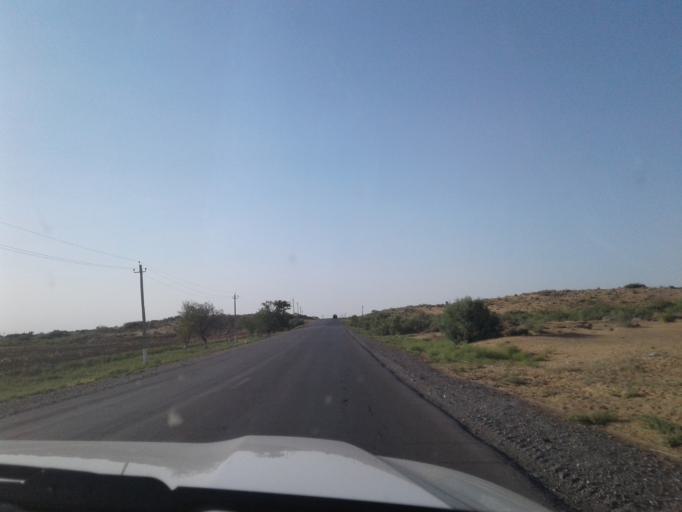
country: TM
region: Mary
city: Yoloeten
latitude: 37.2286
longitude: 62.3739
